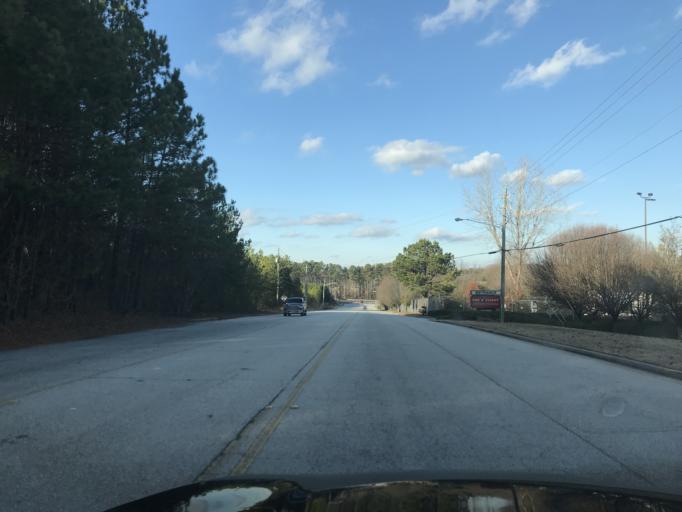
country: US
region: Georgia
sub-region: Fulton County
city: College Park
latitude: 33.6454
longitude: -84.4665
